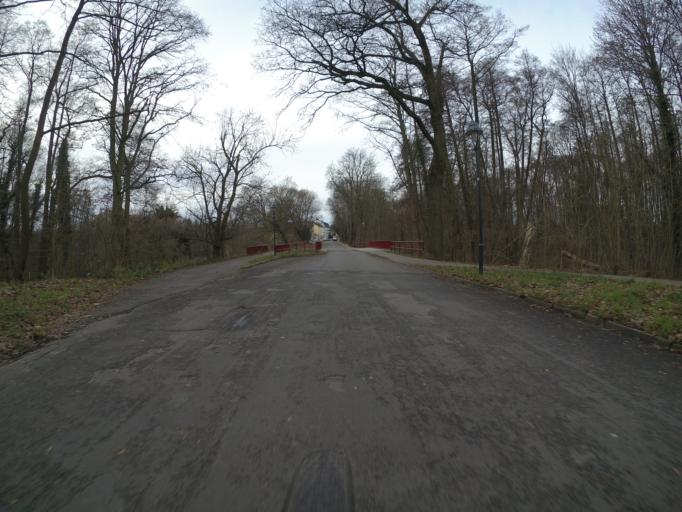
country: DE
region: Brandenburg
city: Hoppegarten
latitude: 52.5014
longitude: 13.6538
